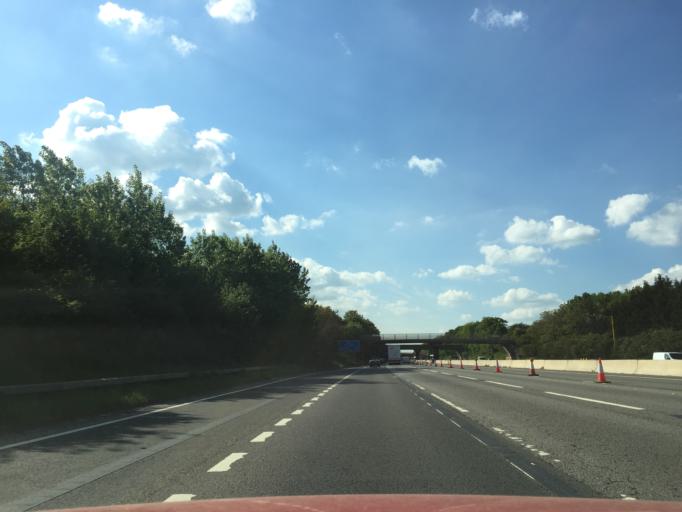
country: GB
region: England
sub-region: Northamptonshire
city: Hardingstone
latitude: 52.1900
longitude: -0.9031
